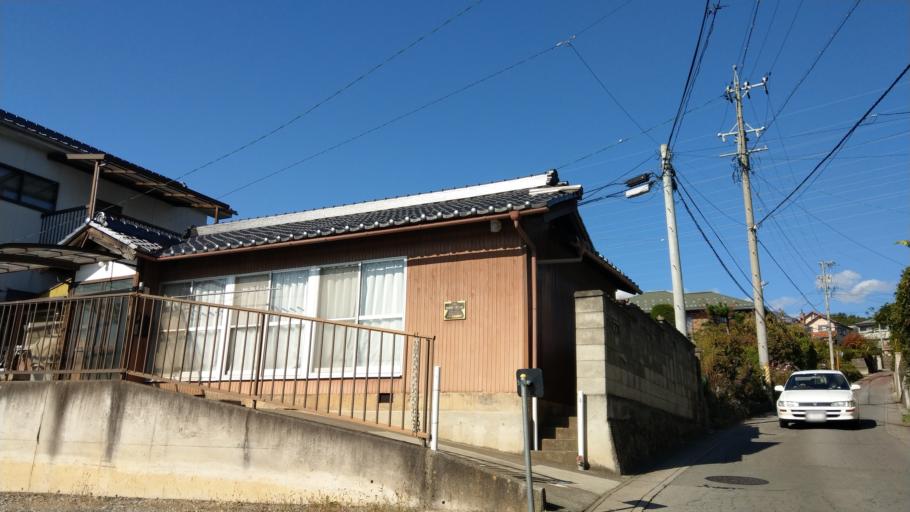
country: JP
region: Nagano
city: Komoro
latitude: 36.3328
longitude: 138.4287
